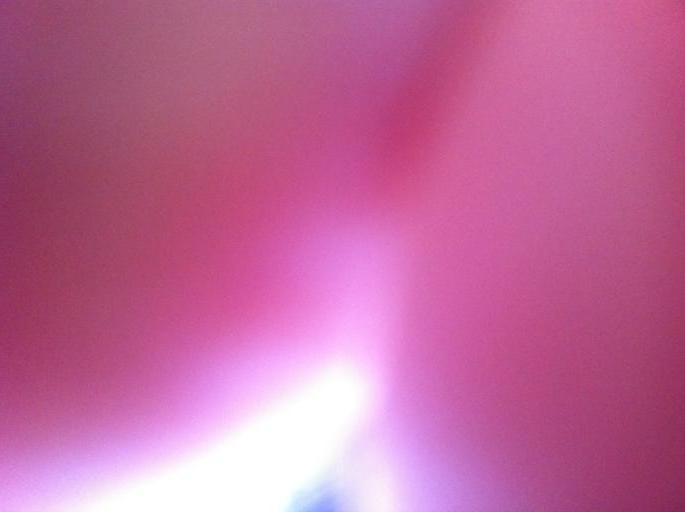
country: CR
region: Guanacaste
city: Hojancha
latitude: 10.0708
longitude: -85.4709
